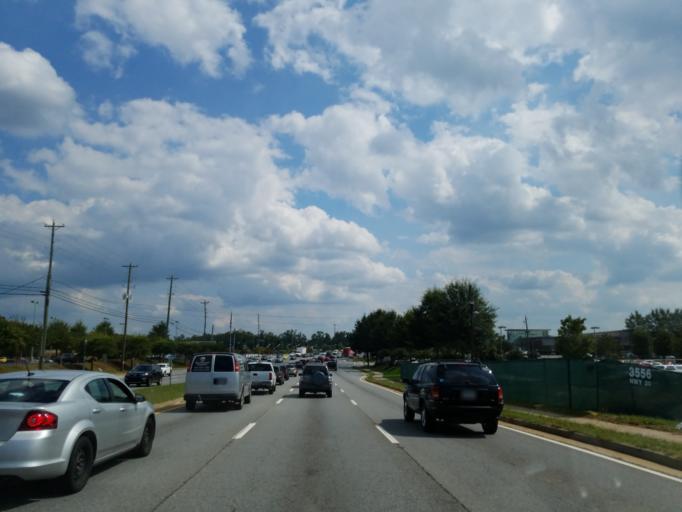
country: US
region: Georgia
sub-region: Gwinnett County
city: Buford
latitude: 34.0798
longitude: -83.9859
